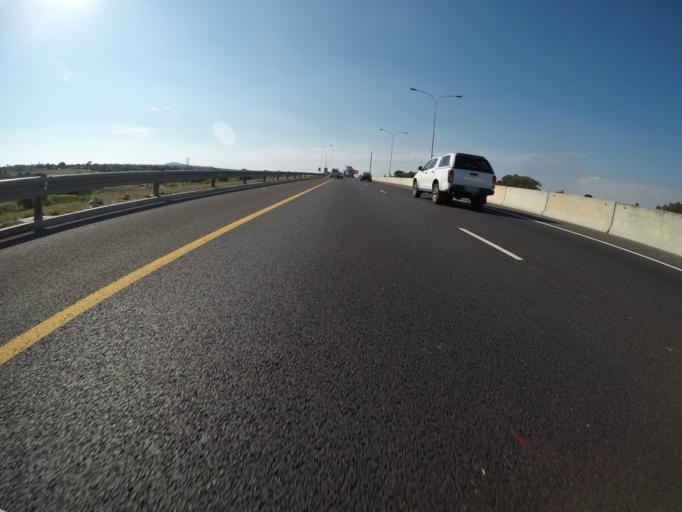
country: ZA
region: Western Cape
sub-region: City of Cape Town
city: Kraaifontein
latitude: -33.8804
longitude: 18.6733
